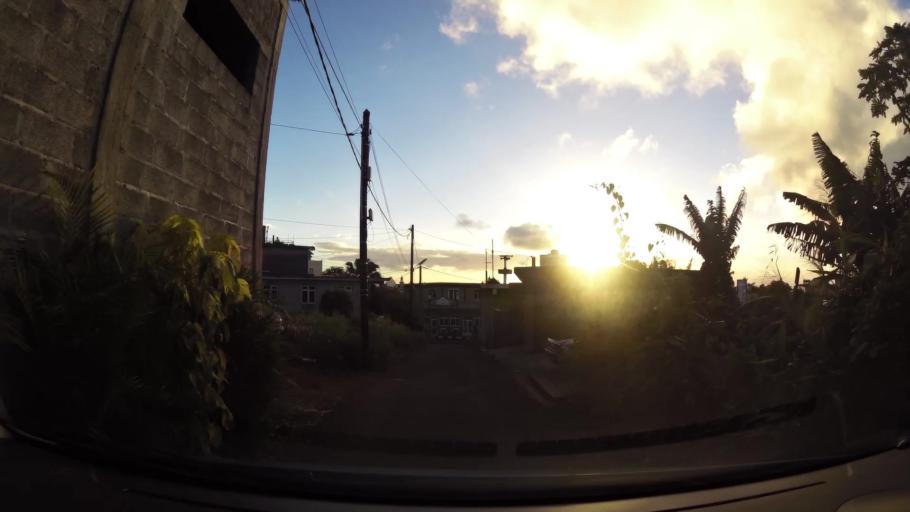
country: MU
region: Plaines Wilhems
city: Curepipe
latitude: -20.3056
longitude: 57.5310
